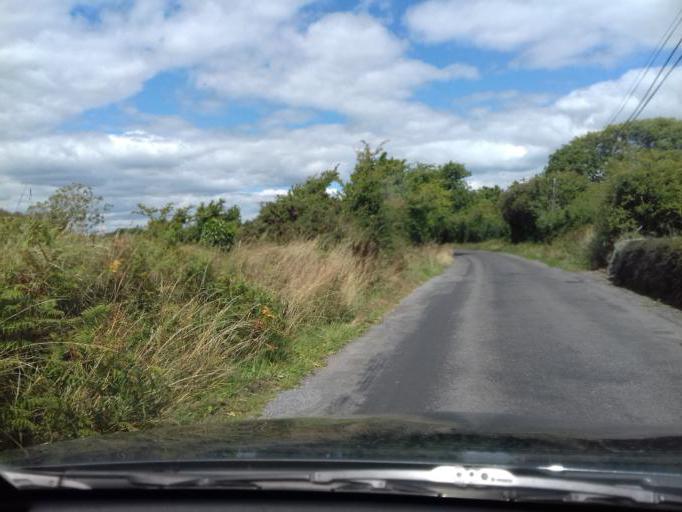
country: IE
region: Munster
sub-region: Waterford
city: Tra Mhor
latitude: 52.1756
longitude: -7.2369
